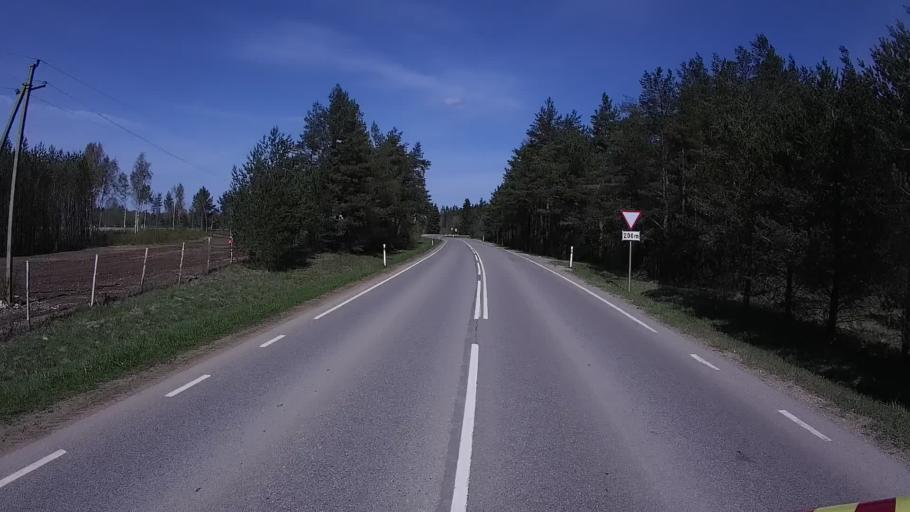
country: EE
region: Harju
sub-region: Keila linn
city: Keila
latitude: 59.3263
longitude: 24.3274
